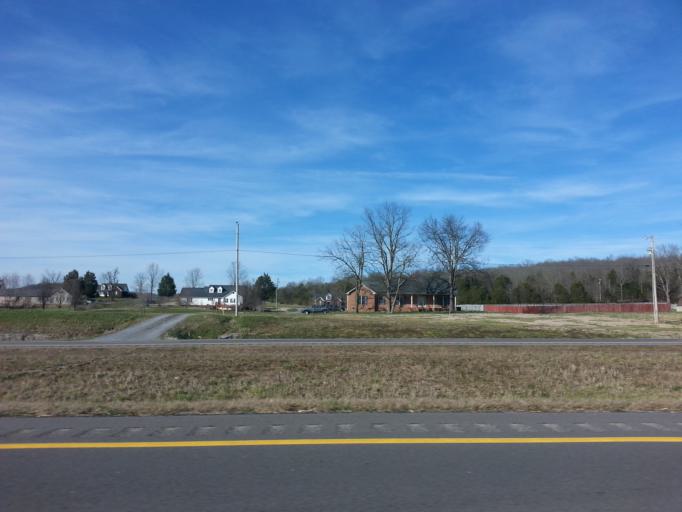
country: US
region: Tennessee
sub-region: Cannon County
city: Woodbury
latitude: 35.8059
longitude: -86.1485
